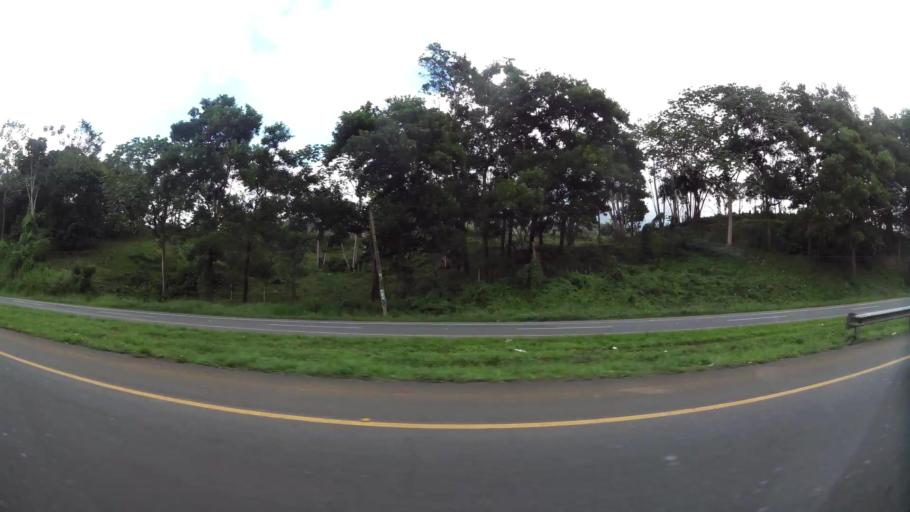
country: DO
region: Monsenor Nouel
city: Piedra Blanca
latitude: 18.8321
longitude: -70.2975
